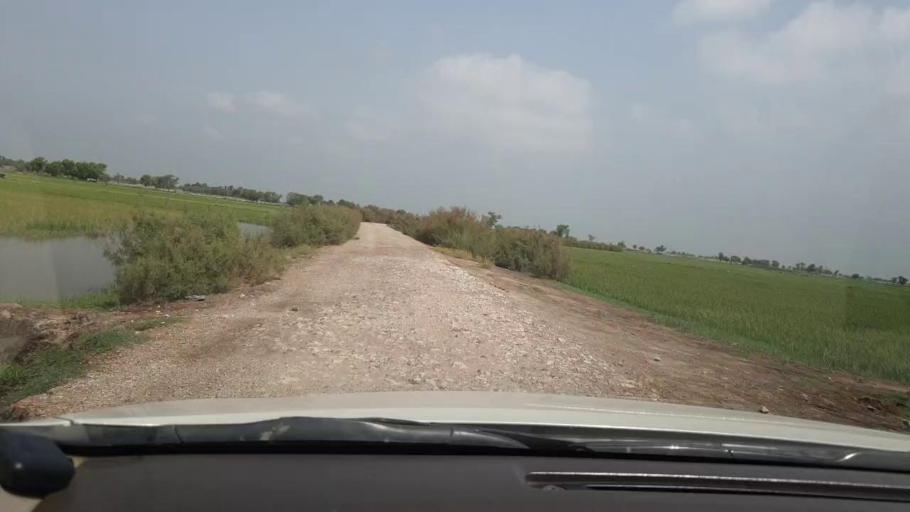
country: PK
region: Sindh
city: Garhi Yasin
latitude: 28.0062
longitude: 68.5399
